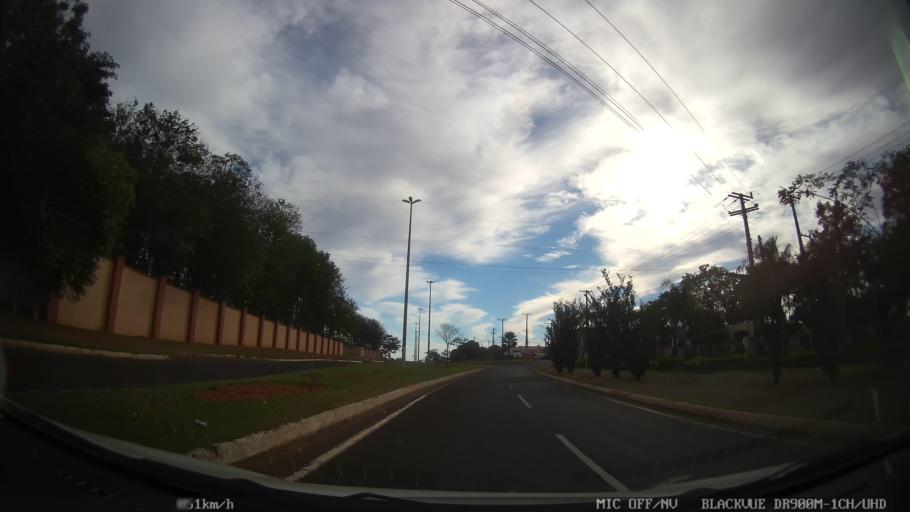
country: BR
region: Sao Paulo
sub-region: Catanduva
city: Catanduva
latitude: -21.1115
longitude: -48.9619
